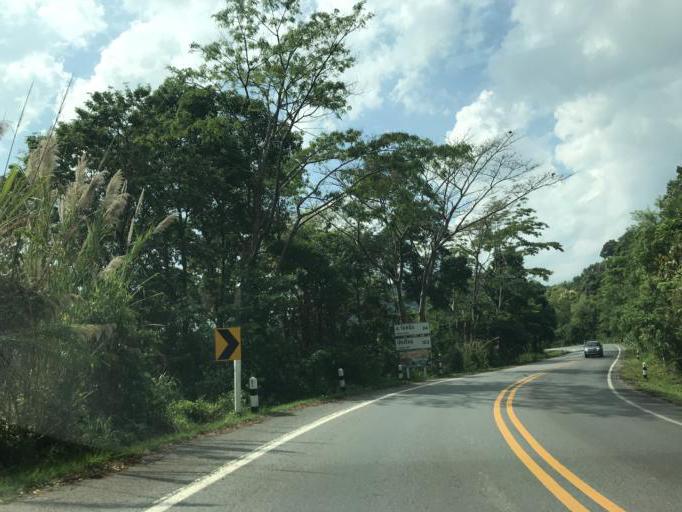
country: TH
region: Phayao
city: Phayao
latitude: 19.0635
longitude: 99.7725
